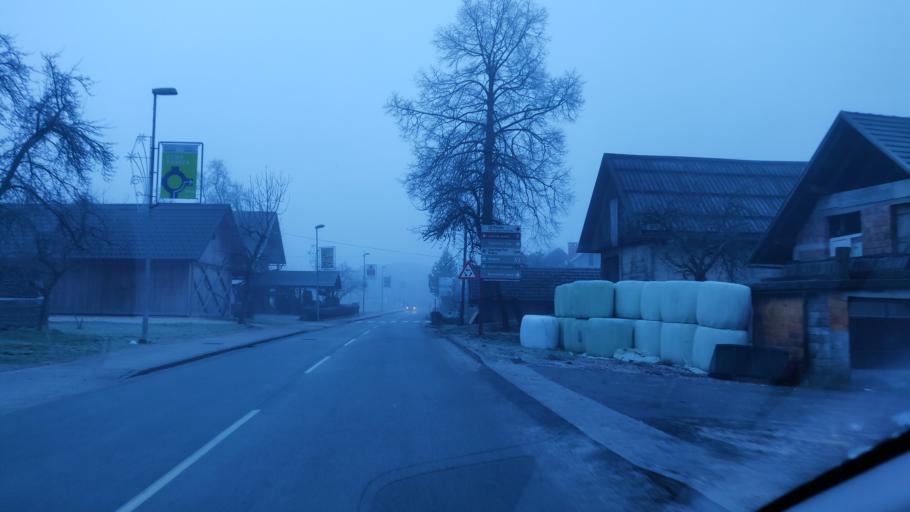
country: SI
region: Bohinj
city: Bohinjska Bistrica
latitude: 46.2747
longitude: 13.9521
